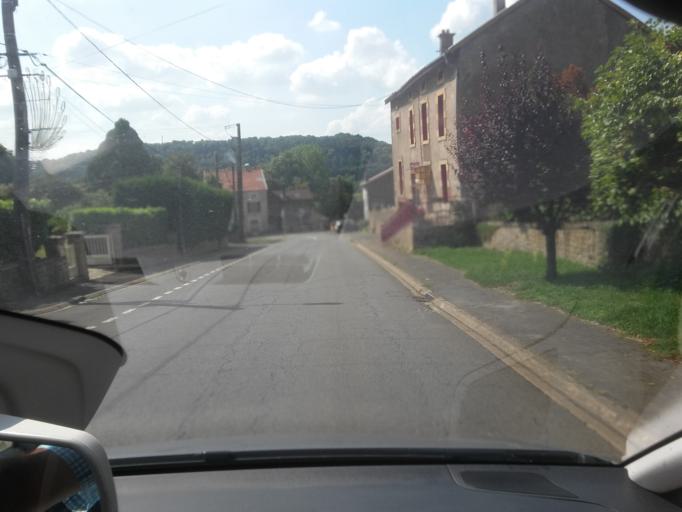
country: BE
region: Wallonia
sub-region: Province du Luxembourg
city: Rouvroy
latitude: 49.4887
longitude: 5.5126
